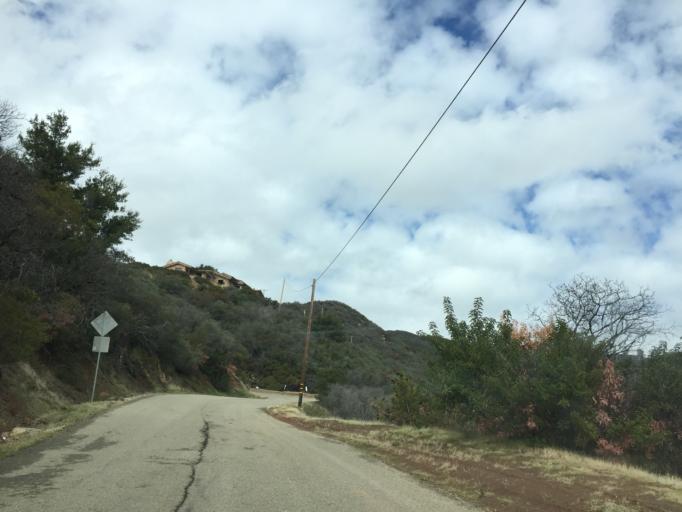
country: US
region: California
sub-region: Santa Barbara County
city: Goleta
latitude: 34.4829
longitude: -119.7977
